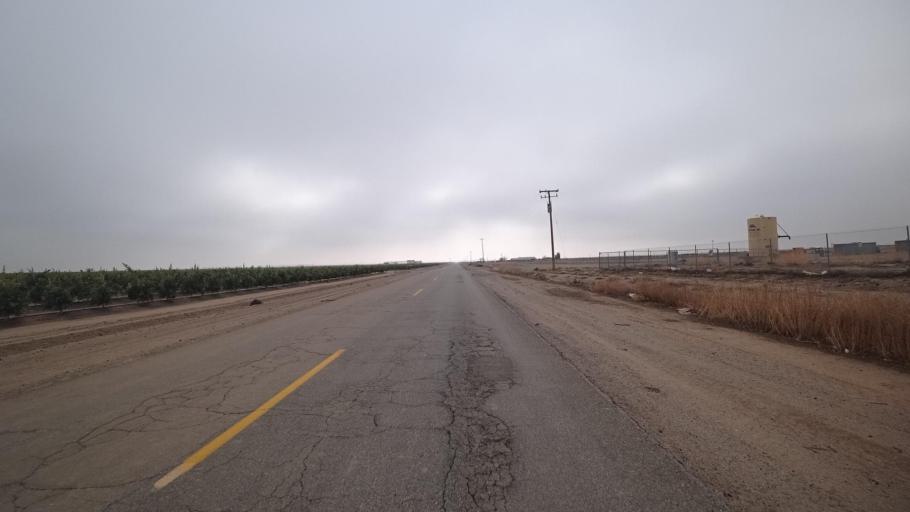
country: US
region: California
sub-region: Kern County
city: Maricopa
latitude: 35.0829
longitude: -119.3140
